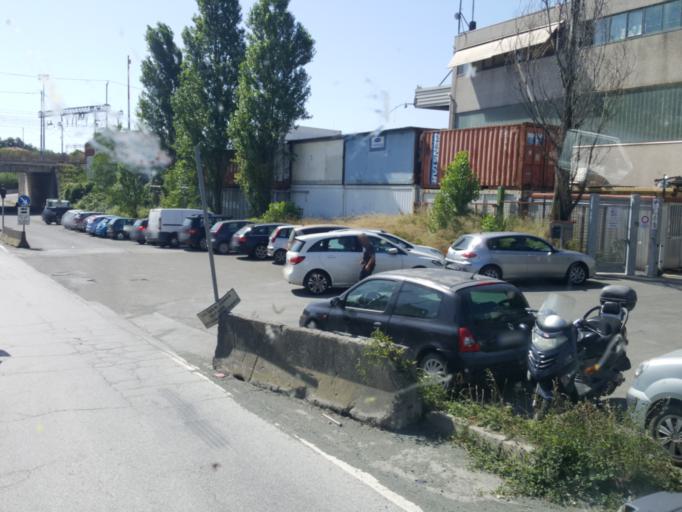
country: IT
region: Liguria
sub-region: Provincia di La Spezia
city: Santo Stefano di Magra
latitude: 44.1511
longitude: 9.9150
